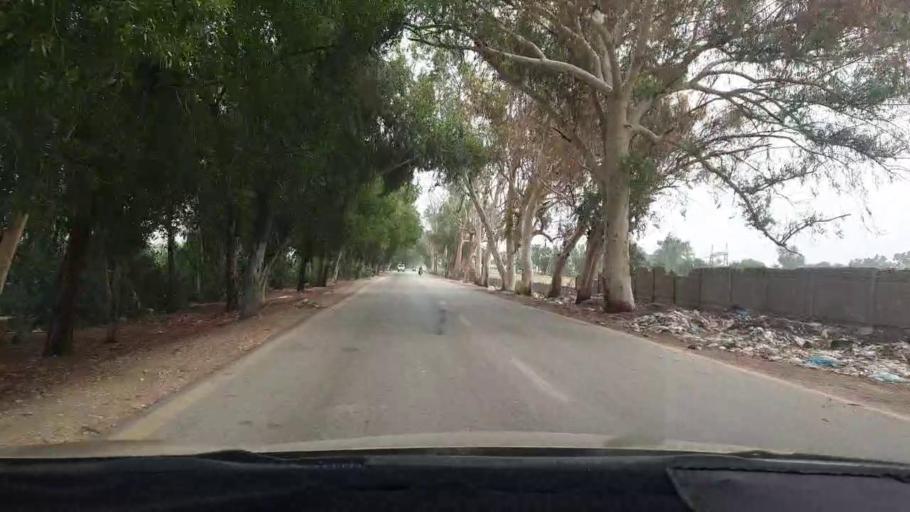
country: PK
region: Sindh
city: Naudero
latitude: 27.6637
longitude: 68.3454
